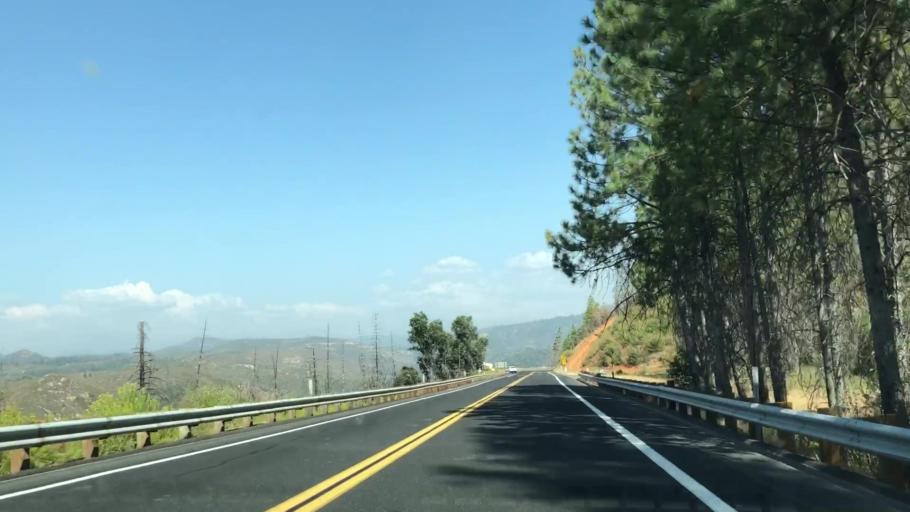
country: US
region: California
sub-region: Tuolumne County
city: Tuolumne City
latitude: 37.8213
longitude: -120.0417
